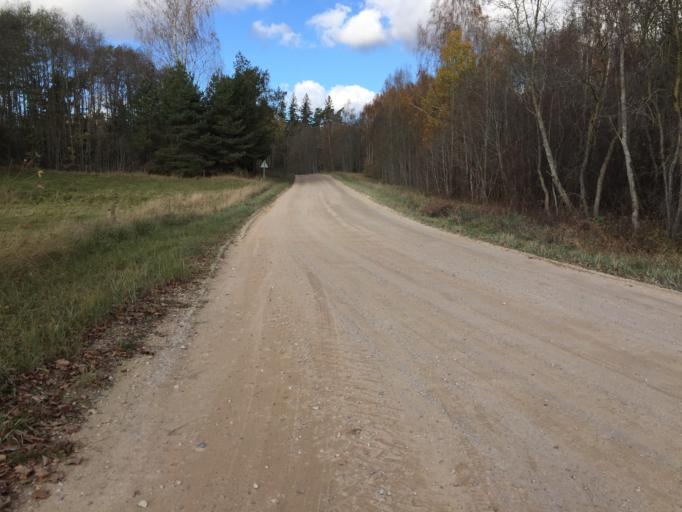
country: LV
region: Tukuma Rajons
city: Tukums
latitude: 56.9604
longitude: 22.9788
